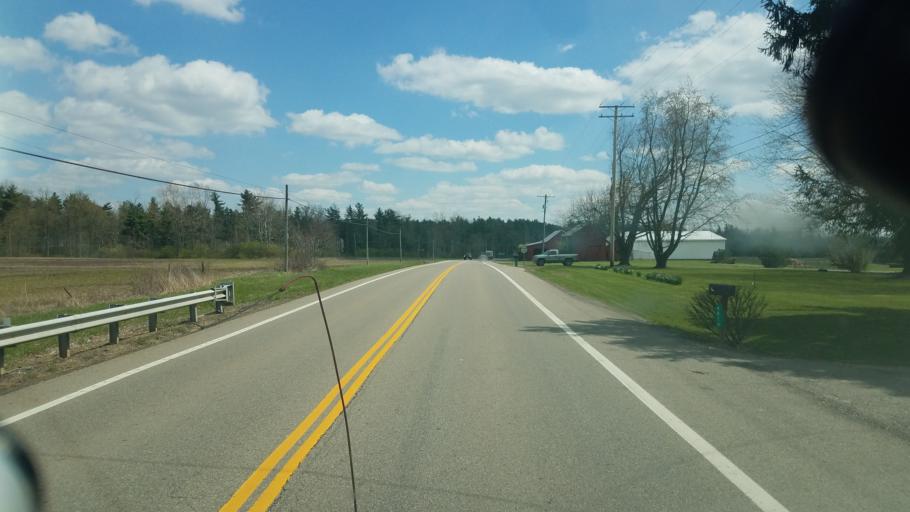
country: US
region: Ohio
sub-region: Licking County
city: Johnstown
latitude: 40.1286
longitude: -82.6606
